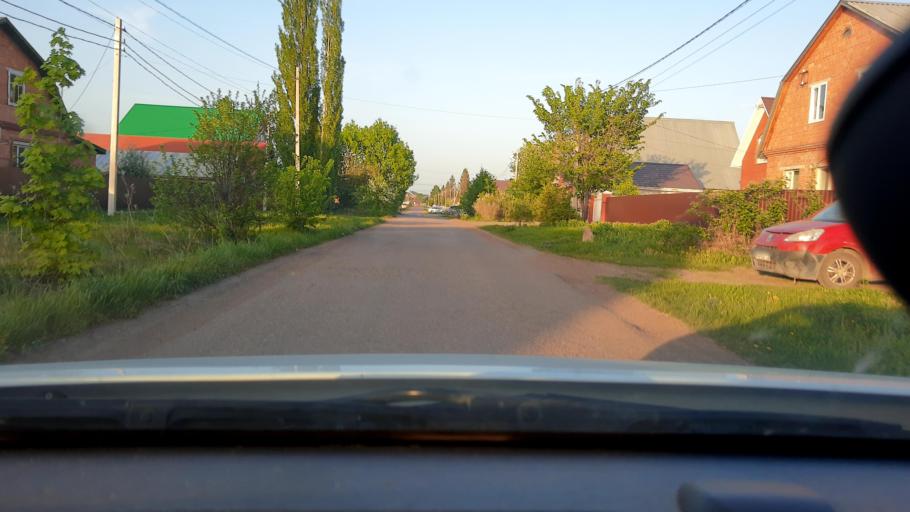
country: RU
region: Bashkortostan
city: Avdon
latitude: 54.4924
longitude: 55.8764
